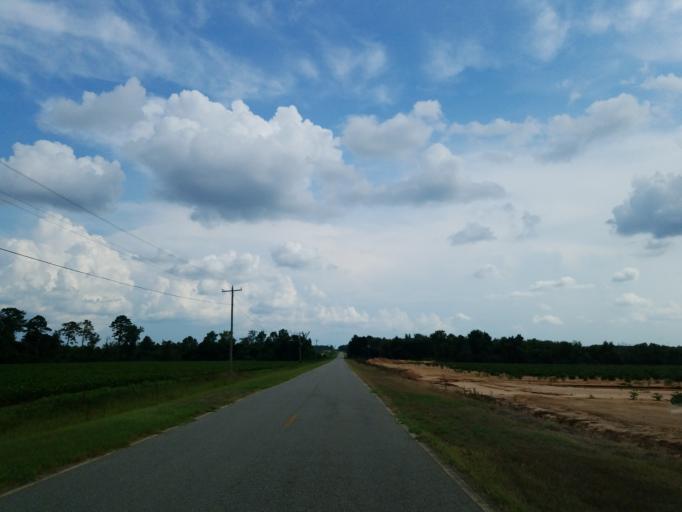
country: US
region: Georgia
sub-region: Dooly County
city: Unadilla
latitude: 32.2742
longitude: -83.7190
